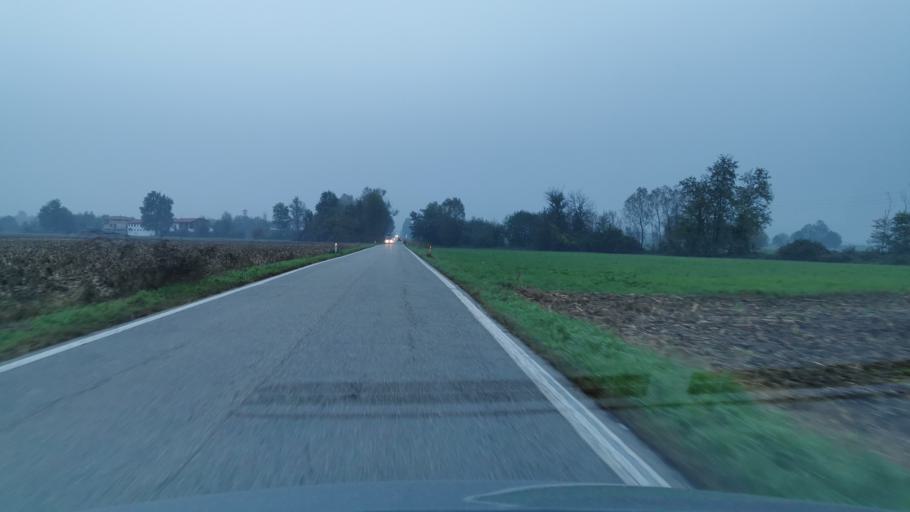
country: IT
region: Piedmont
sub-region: Provincia di Torino
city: Lusiglie
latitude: 45.3227
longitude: 7.7603
